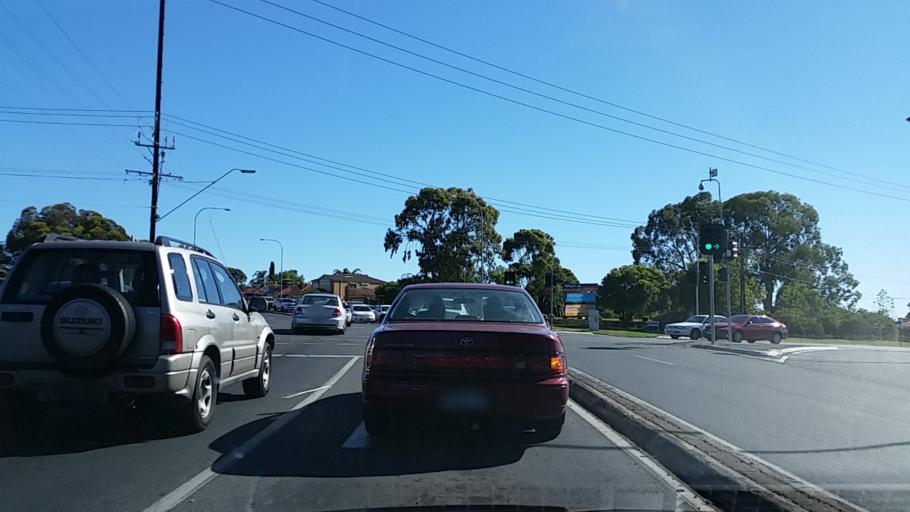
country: AU
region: South Australia
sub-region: Port Adelaide Enfield
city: Enfield
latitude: -34.8470
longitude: 138.6175
